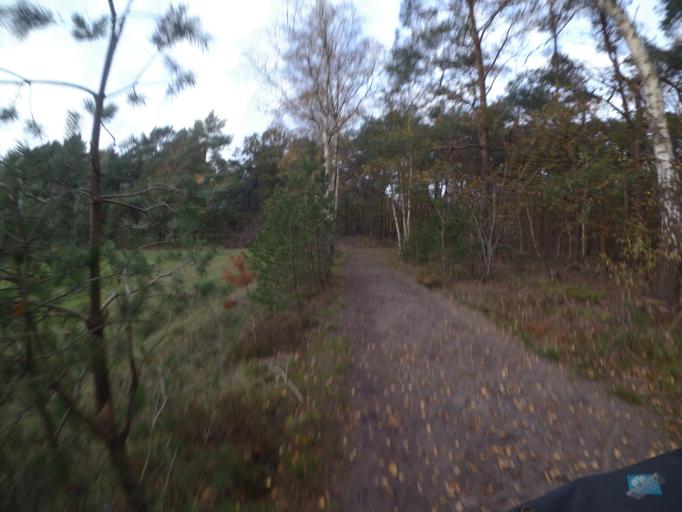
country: NL
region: North Brabant
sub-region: Gemeente Oisterwijk
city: Oisterwijk
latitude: 51.6468
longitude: 5.1662
